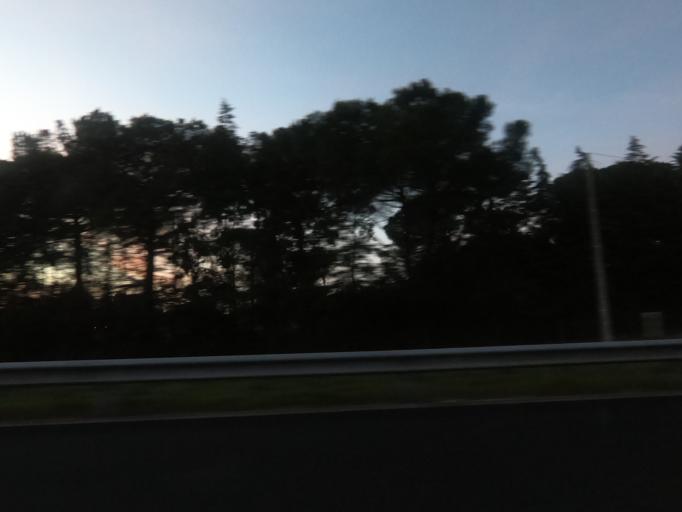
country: PT
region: Santarem
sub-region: Cartaxo
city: Cartaxo
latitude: 39.2237
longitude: -8.7698
